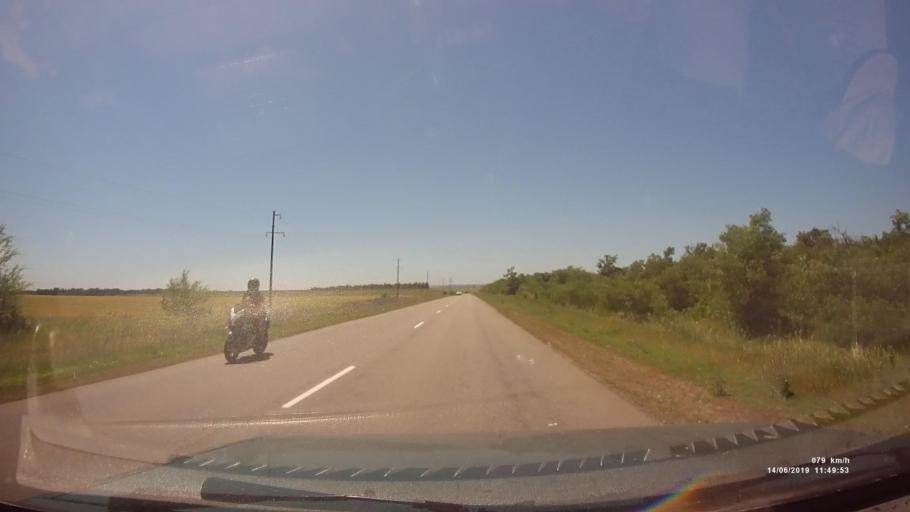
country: RU
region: Rostov
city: Kazanskaya
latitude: 49.8509
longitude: 41.2730
